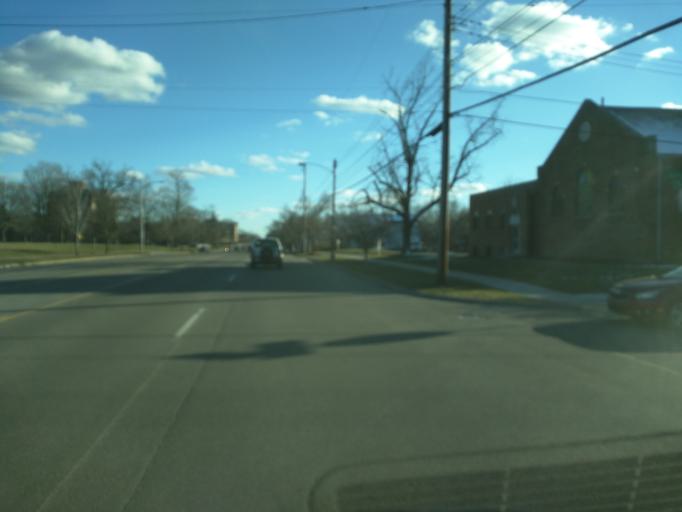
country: US
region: Michigan
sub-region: Ingham County
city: Lansing
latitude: 42.7391
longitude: -84.5379
